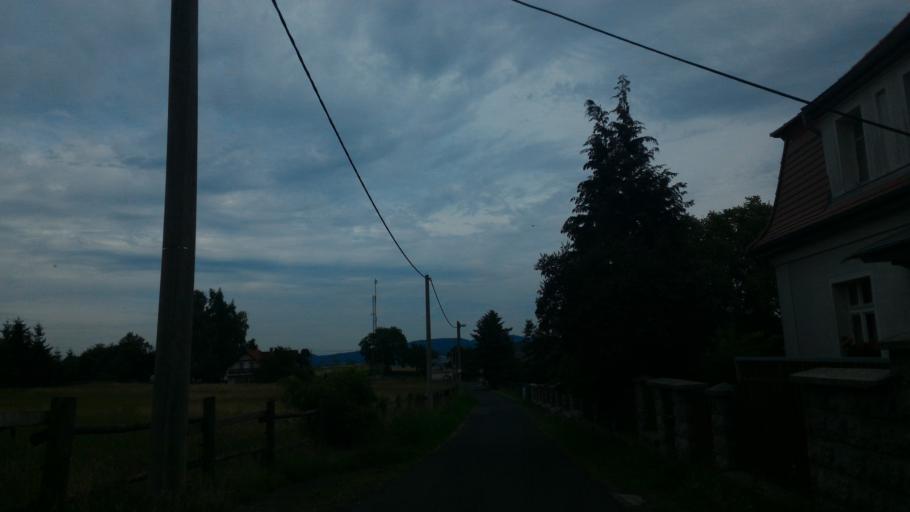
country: CZ
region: Ustecky
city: Varnsdorf
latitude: 50.9178
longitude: 14.6400
